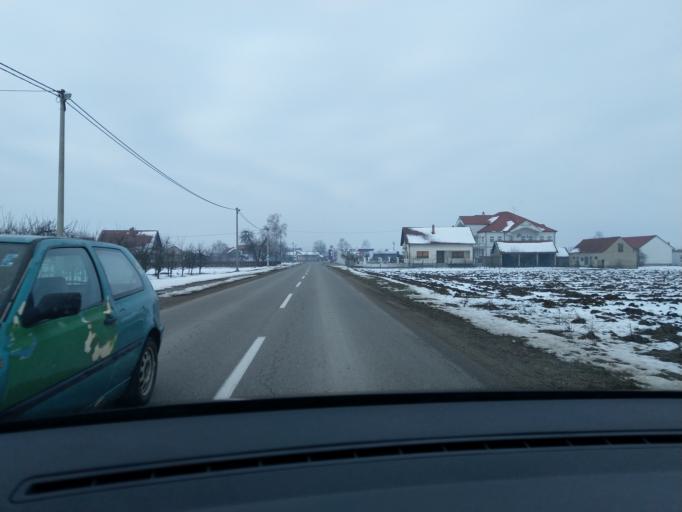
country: BA
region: Republika Srpska
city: Velika Obarska
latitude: 44.7909
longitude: 19.1807
